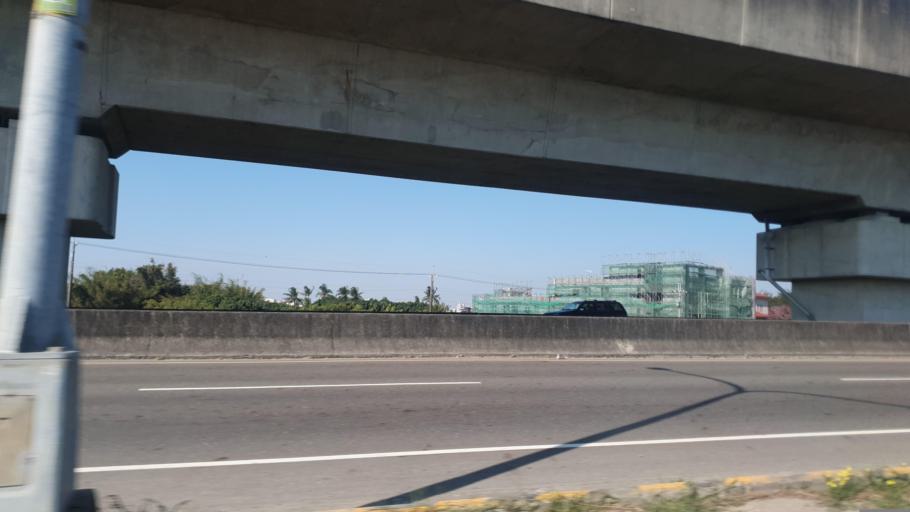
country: TW
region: Taiwan
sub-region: Tainan
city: Tainan
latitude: 23.0148
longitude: 120.2884
